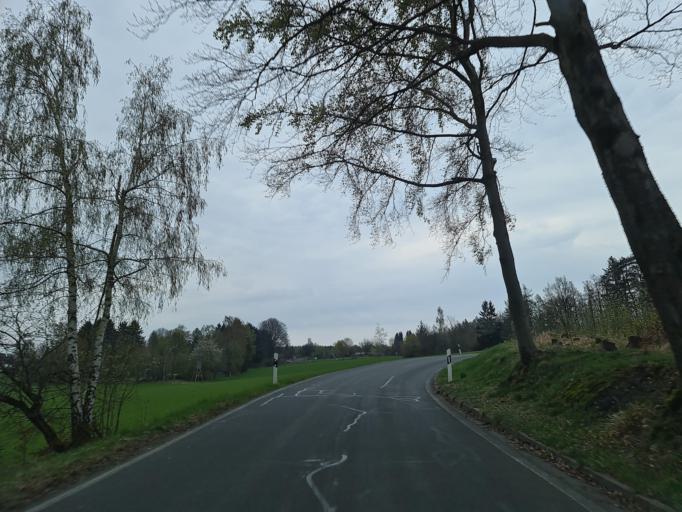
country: DE
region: Saxony
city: Ellefeld
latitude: 50.4694
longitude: 12.3844
